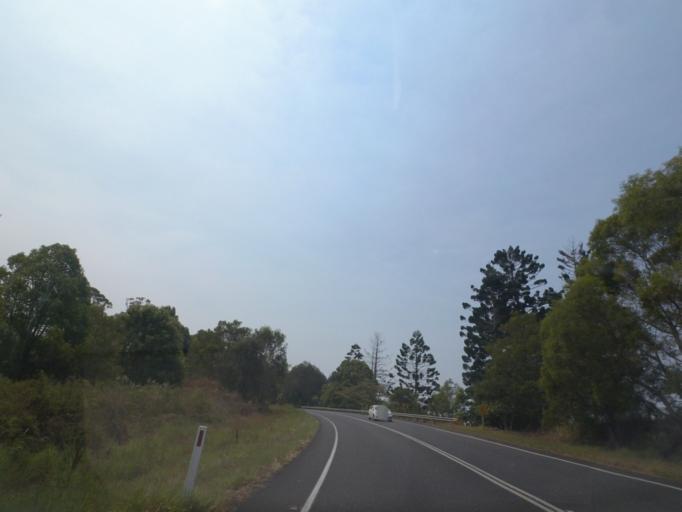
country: AU
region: New South Wales
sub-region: Byron Shire
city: Brunswick Heads
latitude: -28.4928
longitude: 153.5256
